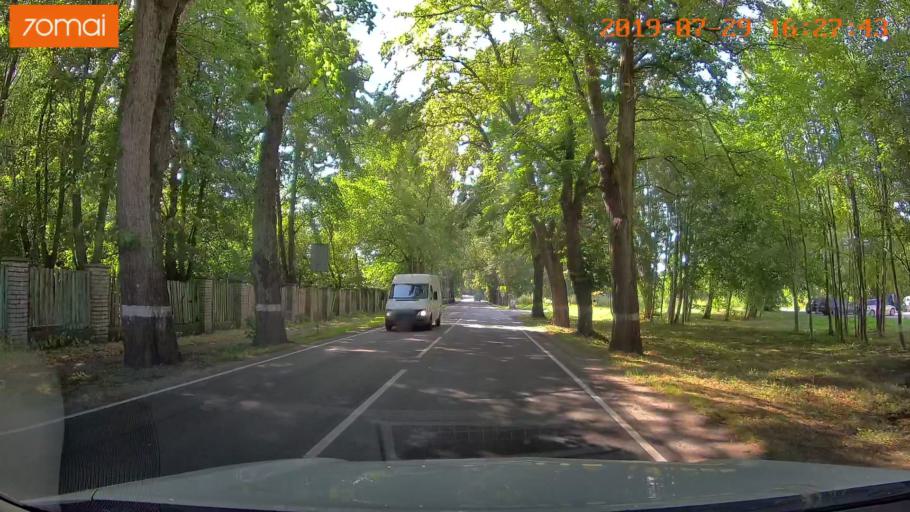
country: RU
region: Kaliningrad
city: Primorsk
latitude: 54.7302
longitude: 19.9899
